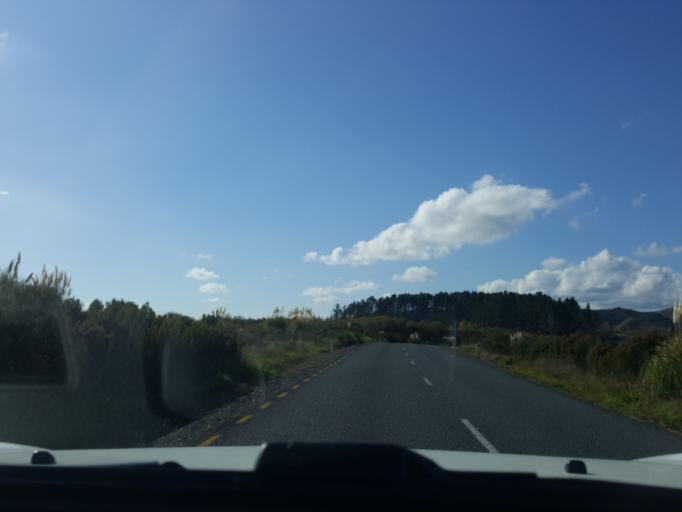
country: NZ
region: Waikato
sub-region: Waikato District
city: Ngaruawahia
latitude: -37.5347
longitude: 175.1779
